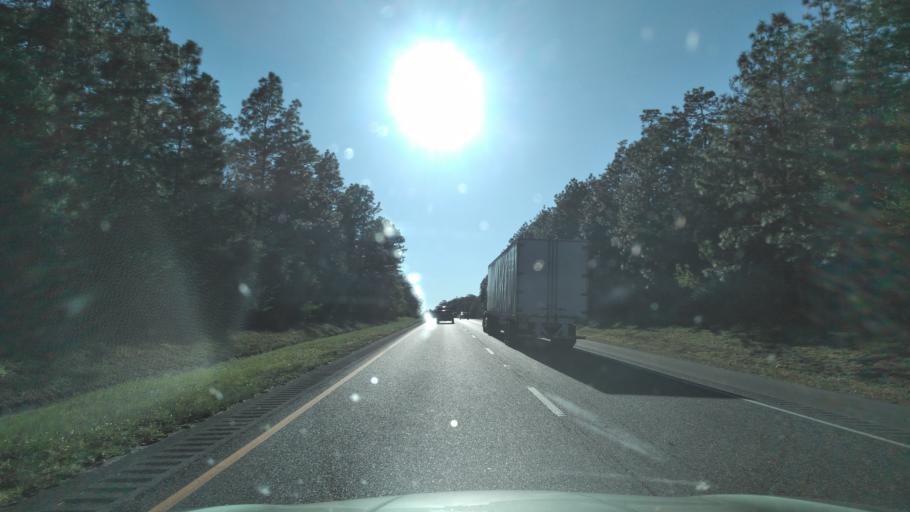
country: US
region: Alabama
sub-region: Escambia County
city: Atmore
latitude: 31.0632
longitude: -87.5703
